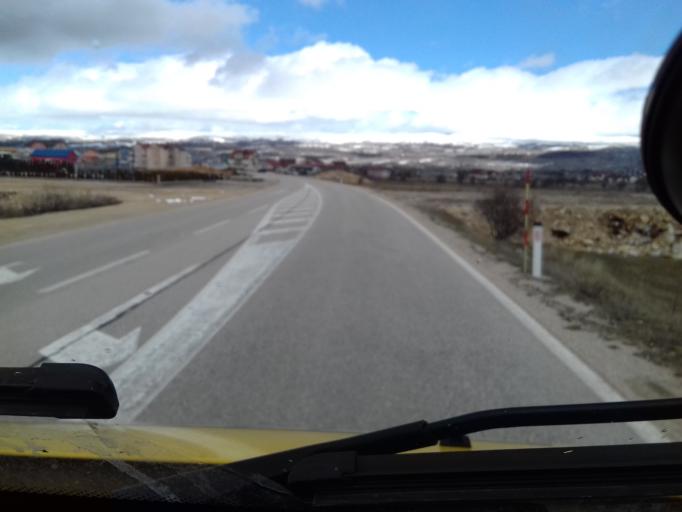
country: BA
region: Federation of Bosnia and Herzegovina
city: Tomislavgrad
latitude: 43.7094
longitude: 17.2371
